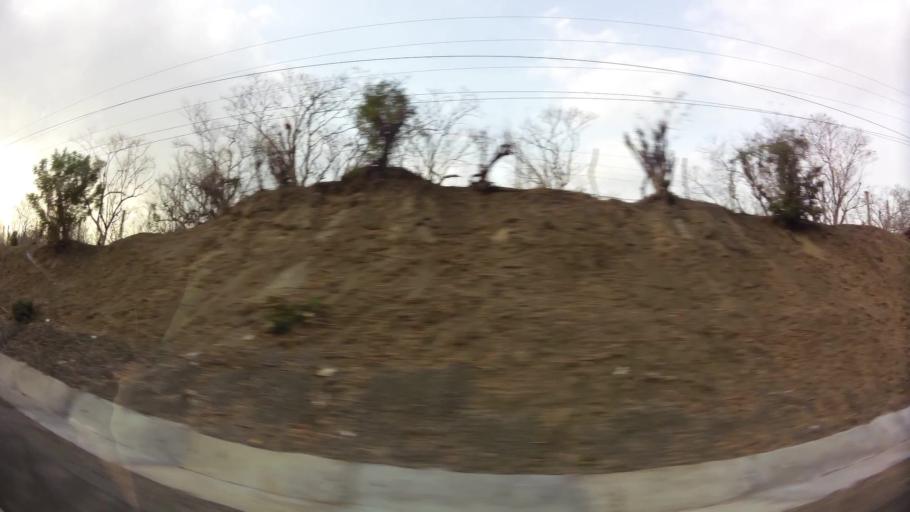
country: NI
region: Leon
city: Nagarote
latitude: 12.2598
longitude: -86.4630
